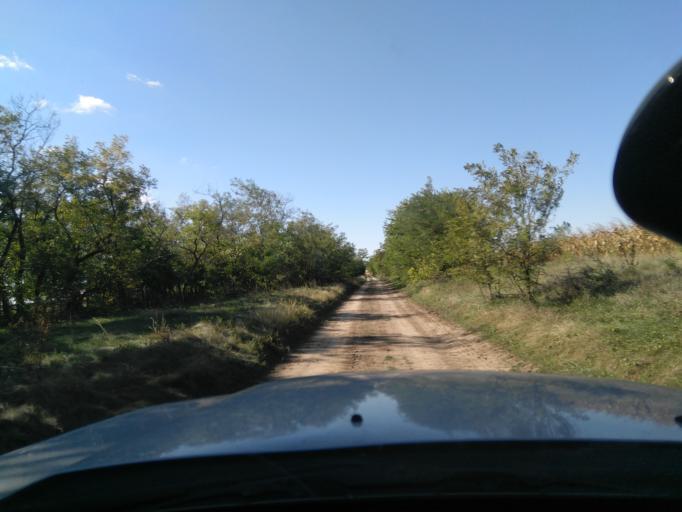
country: HU
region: Fejer
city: Baracska
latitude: 47.3102
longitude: 18.7095
